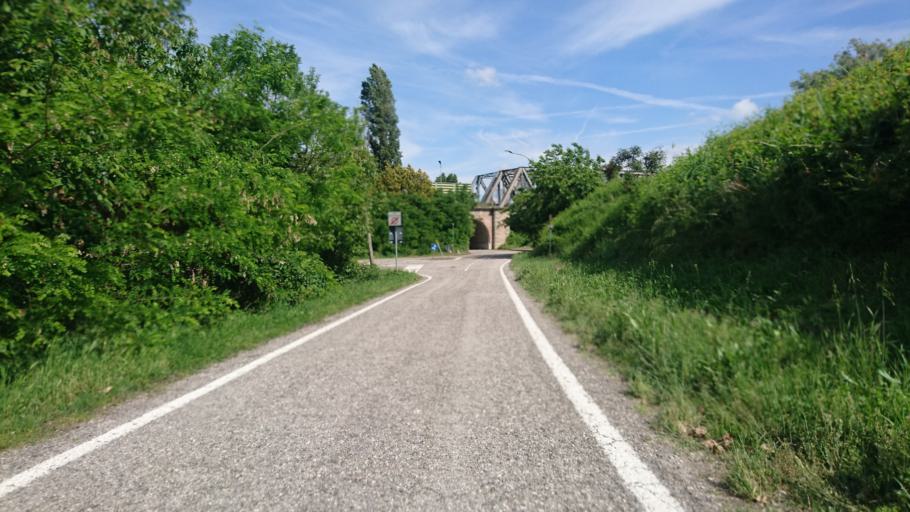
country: IT
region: Lombardy
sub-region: Provincia di Mantova
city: Revere
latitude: 45.0537
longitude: 11.1334
